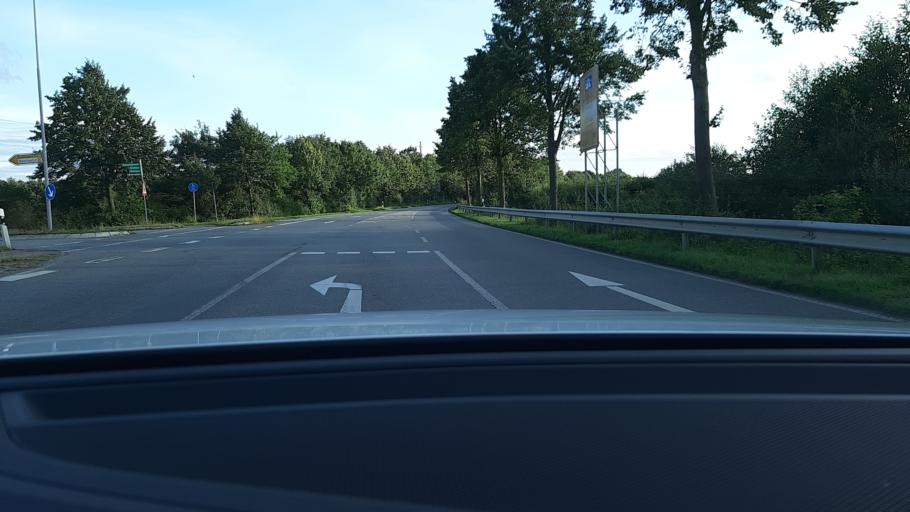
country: DE
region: Schleswig-Holstein
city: Stockelsdorf
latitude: 53.9053
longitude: 10.6405
